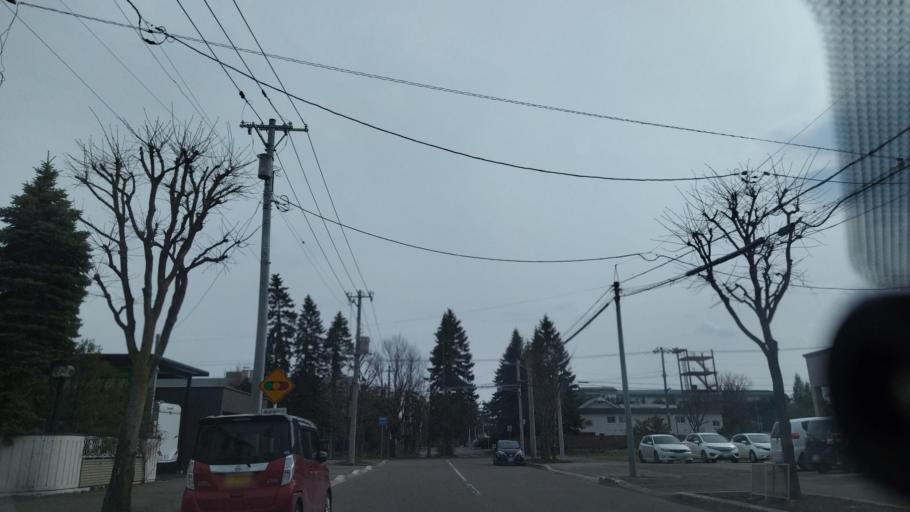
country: JP
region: Hokkaido
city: Obihiro
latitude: 42.9218
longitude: 143.2166
